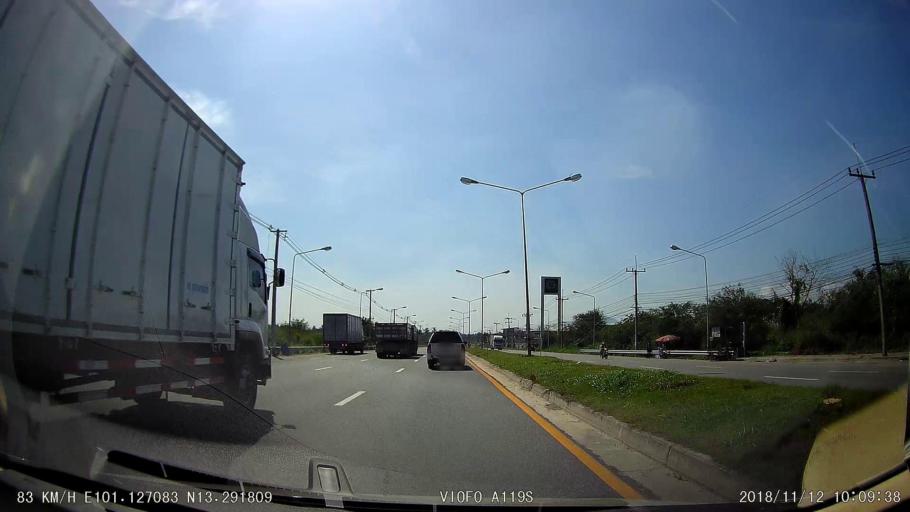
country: TH
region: Chon Buri
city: Ban Bueng
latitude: 13.2915
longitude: 101.1272
